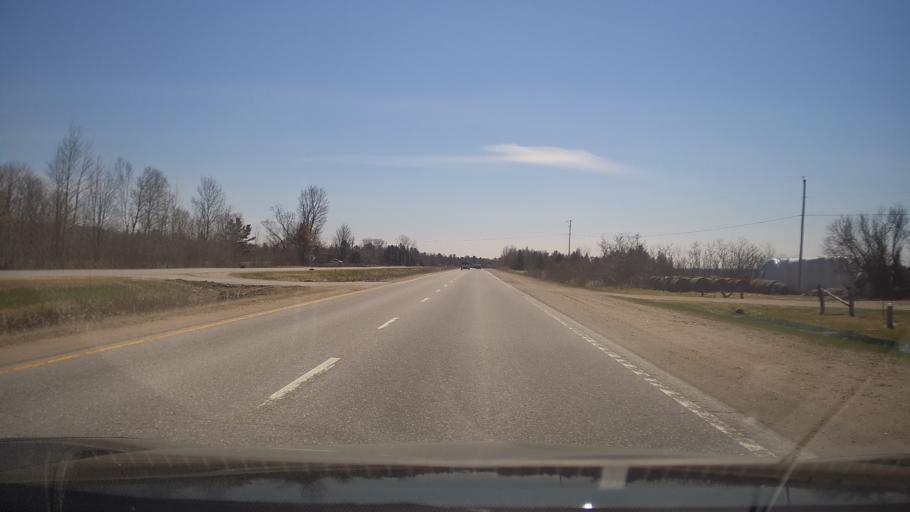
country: CA
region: Quebec
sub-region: Outaouais
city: Wakefield
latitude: 45.5207
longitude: -75.9889
